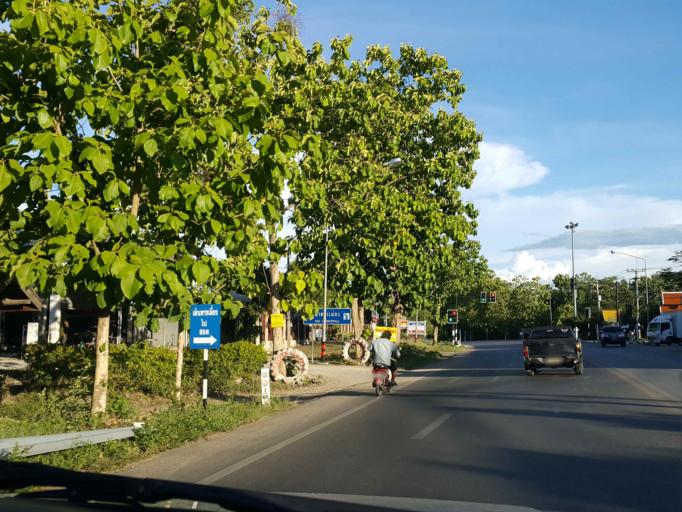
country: TH
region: Chiang Mai
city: Chom Thong
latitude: 18.4382
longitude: 98.6795
